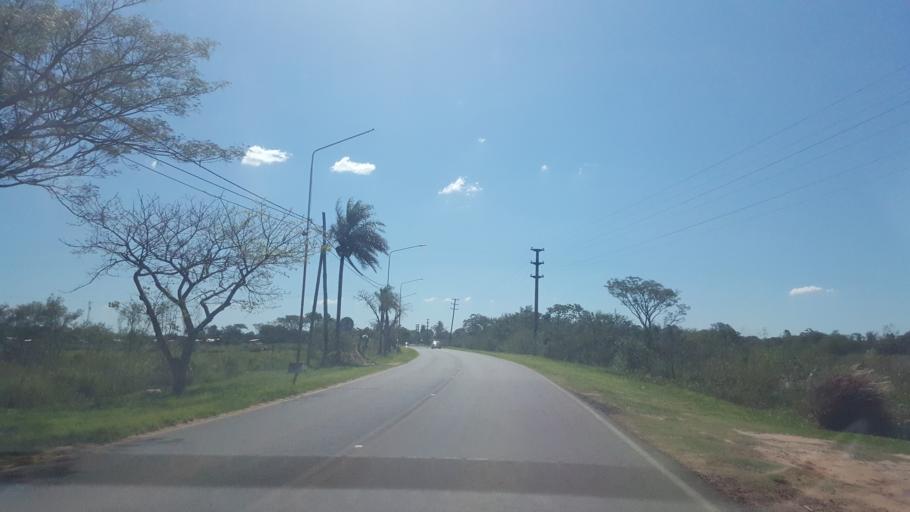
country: AR
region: Corrientes
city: Ituzaingo
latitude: -27.5945
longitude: -56.6798
